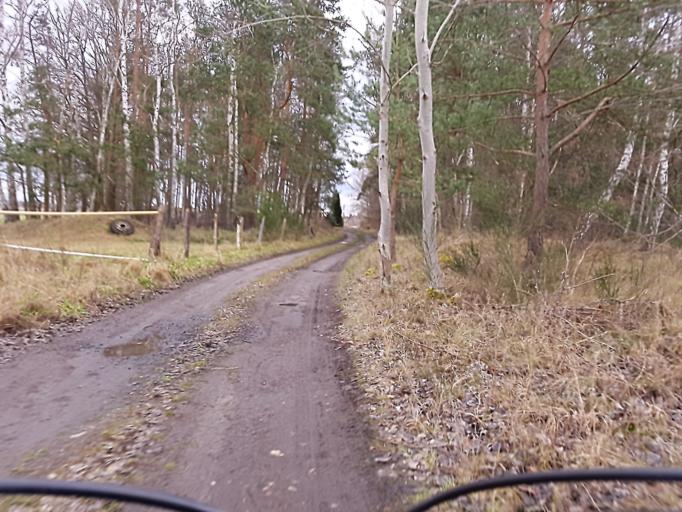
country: DE
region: Brandenburg
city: Schilda
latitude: 51.5910
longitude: 13.3749
